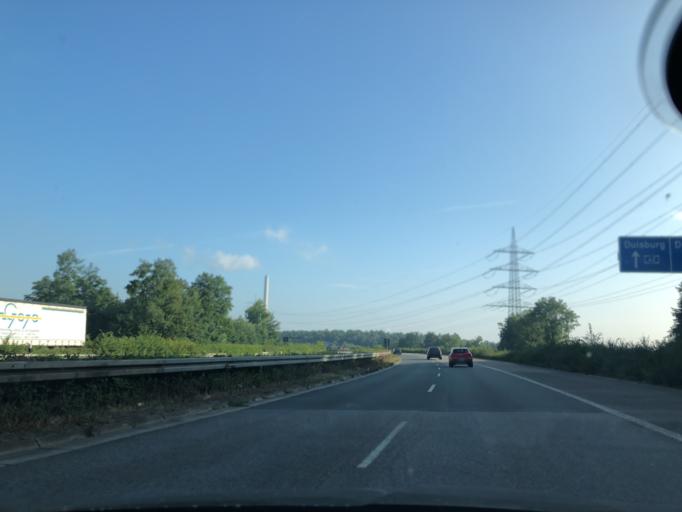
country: DE
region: North Rhine-Westphalia
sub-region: Regierungsbezirk Dusseldorf
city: Essen
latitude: 51.5023
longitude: 6.9968
